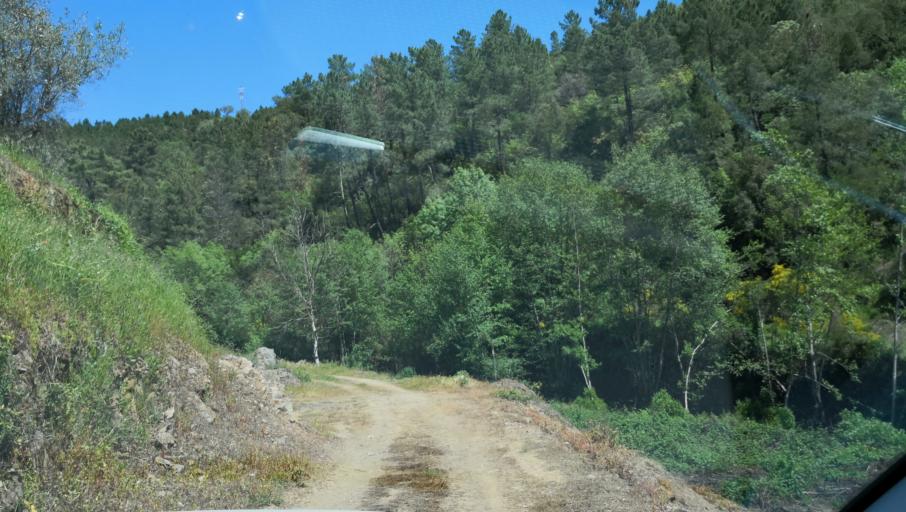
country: PT
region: Vila Real
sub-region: Vila Real
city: Vila Real
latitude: 41.2295
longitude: -7.7165
